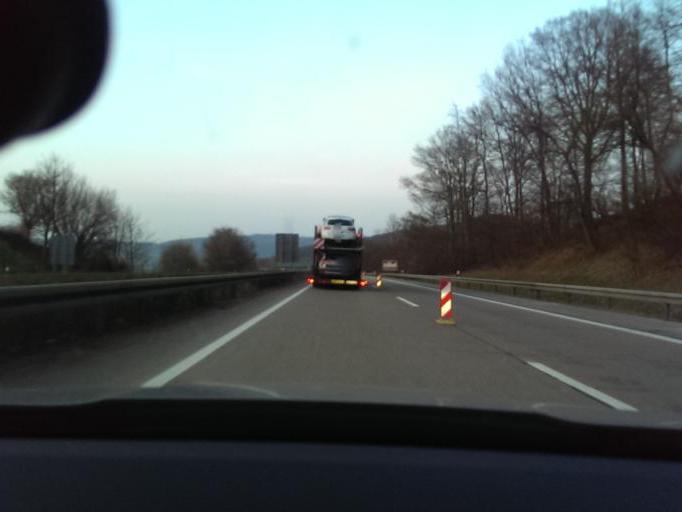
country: DE
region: Lower Saxony
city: Kalefeld
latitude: 51.7665
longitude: 10.0221
